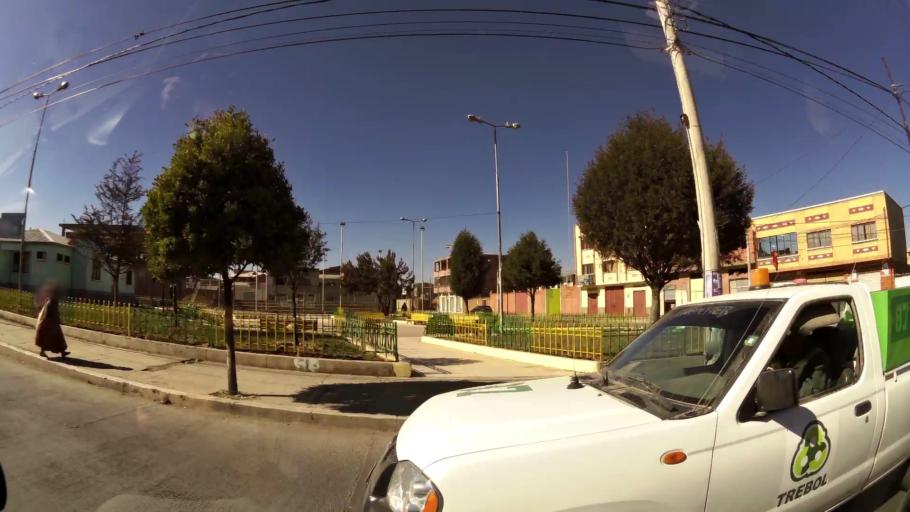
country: BO
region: La Paz
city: La Paz
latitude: -16.5231
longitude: -68.1951
